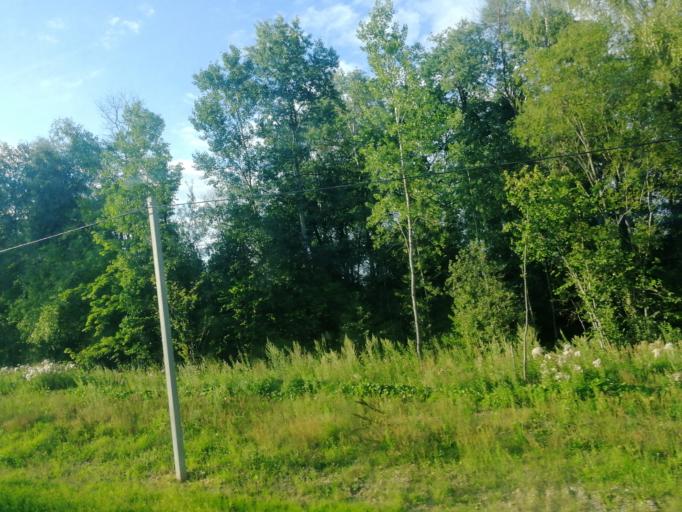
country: RU
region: Kaluga
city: Kaluga
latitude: 54.4407
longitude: 36.3303
